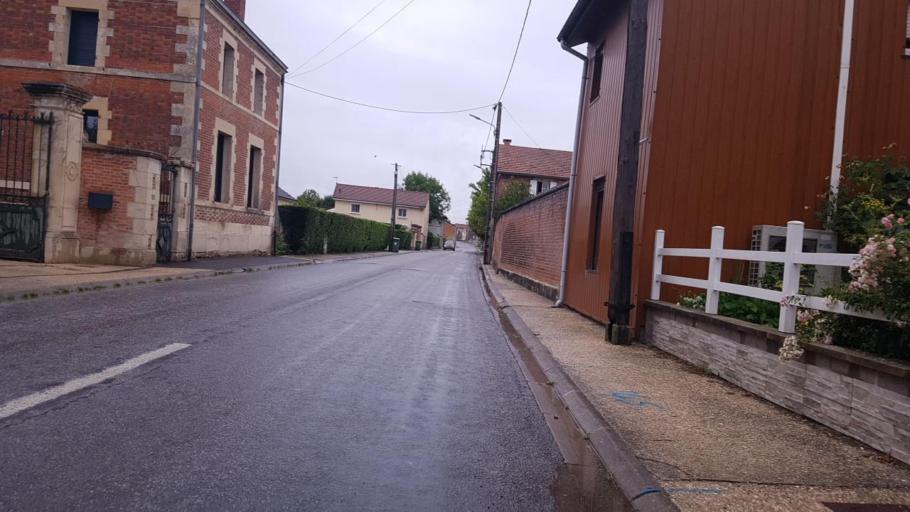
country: FR
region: Champagne-Ardenne
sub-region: Departement de la Marne
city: Sarry
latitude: 48.9062
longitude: 4.4289
